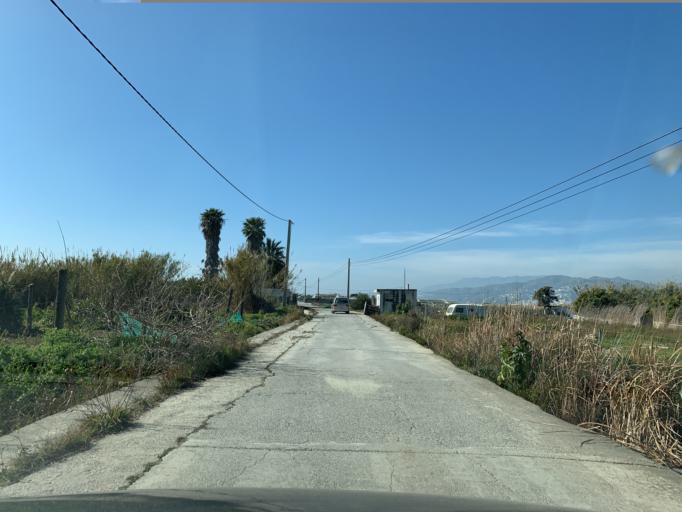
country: ES
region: Andalusia
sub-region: Provincia de Granada
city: El Varadero
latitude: 36.7260
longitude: -3.5516
